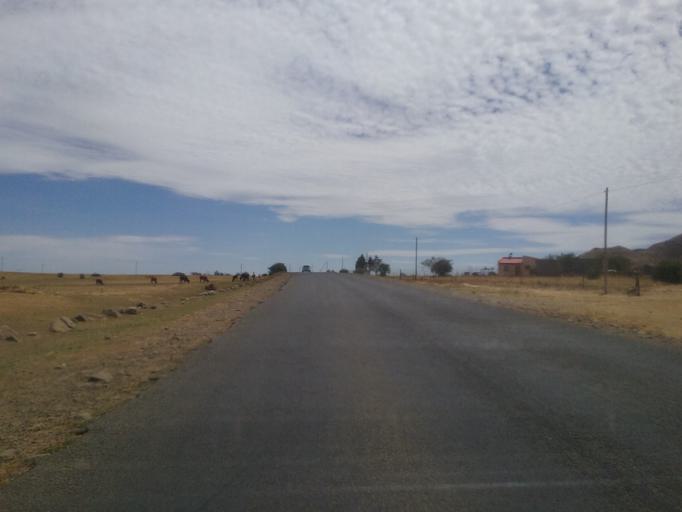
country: LS
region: Mafeteng
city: Mafeteng
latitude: -29.8609
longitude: 27.2355
